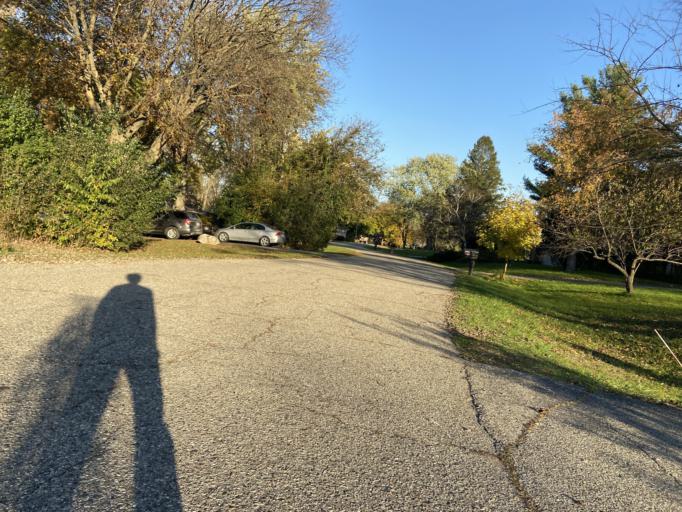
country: US
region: Michigan
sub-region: Oakland County
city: Franklin
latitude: 42.5307
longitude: -83.3384
